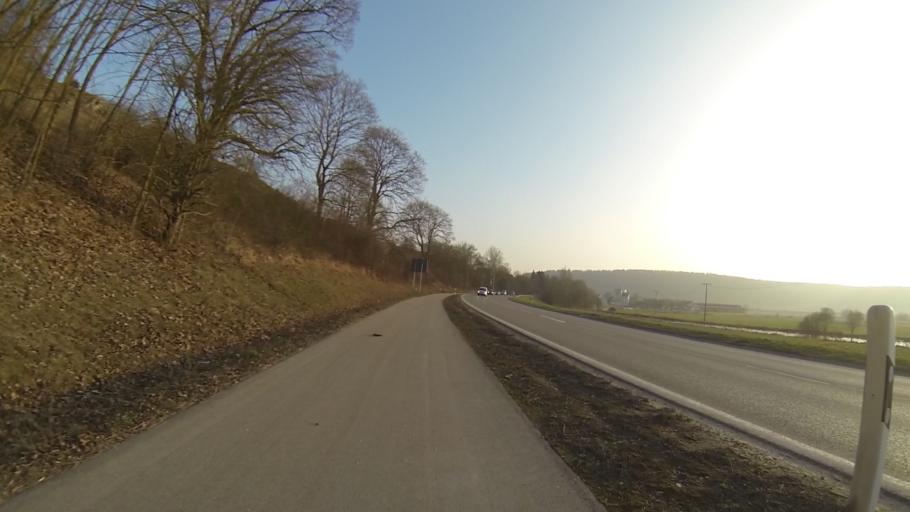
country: DE
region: Baden-Wuerttemberg
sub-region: Regierungsbezirk Stuttgart
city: Heidenheim an der Brenz
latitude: 48.7257
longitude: 10.1577
